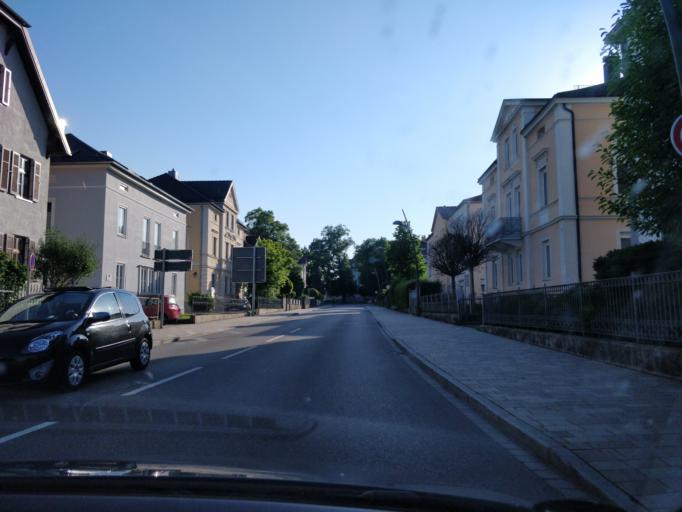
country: DE
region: Bavaria
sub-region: Swabia
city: Noerdlingen
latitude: 48.8494
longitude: 10.4962
